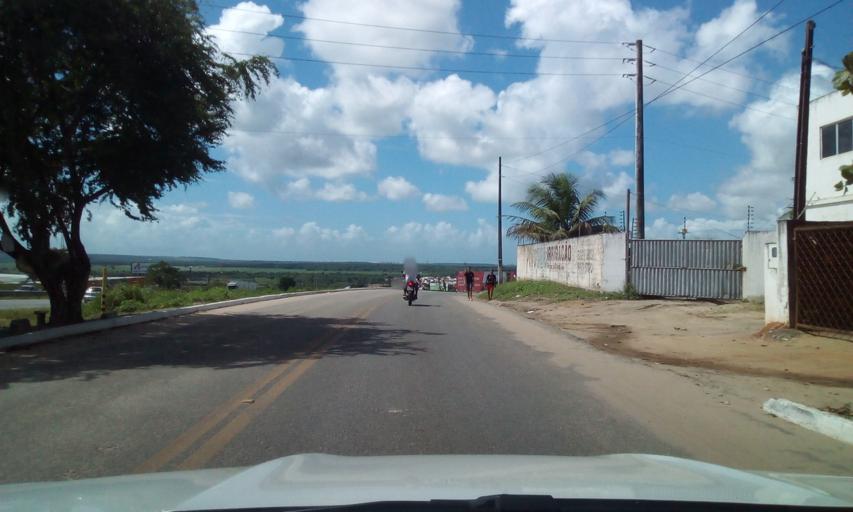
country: BR
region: Paraiba
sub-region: Bayeux
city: Bayeux
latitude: -7.1271
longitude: -34.9499
